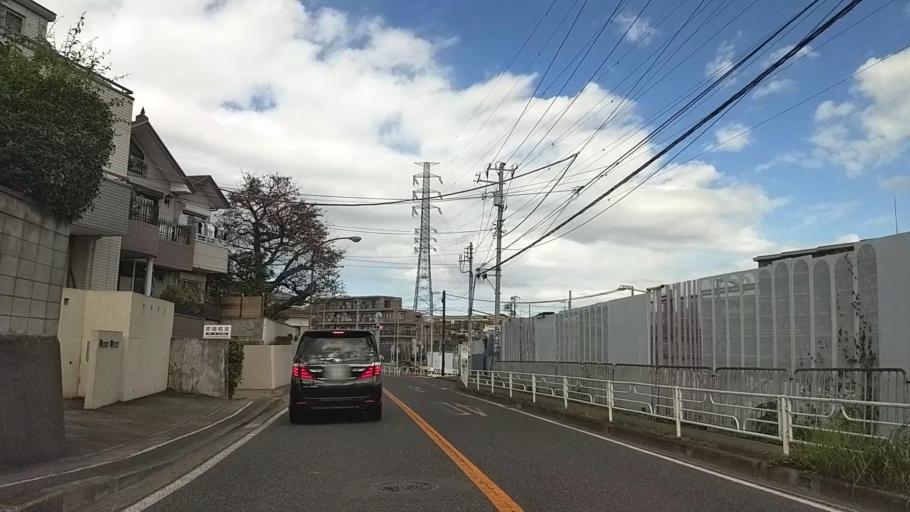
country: JP
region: Kanagawa
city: Yokohama
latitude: 35.5074
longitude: 139.6396
